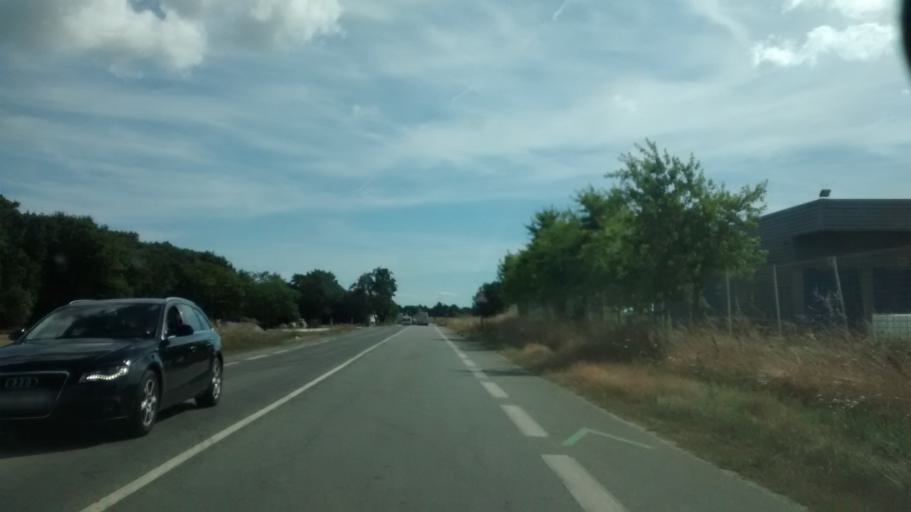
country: FR
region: Pays de la Loire
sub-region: Departement de la Loire-Atlantique
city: Pont-Saint-Martin
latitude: 47.1512
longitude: -1.6007
